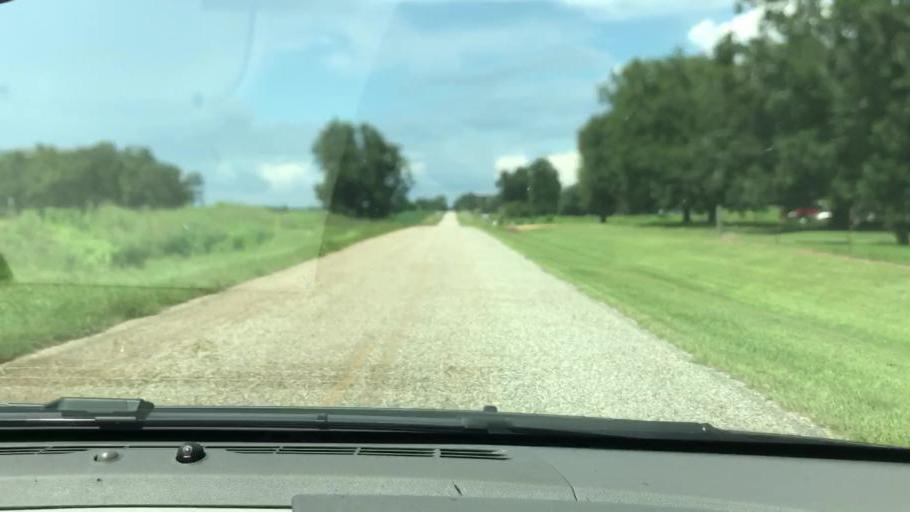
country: US
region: Georgia
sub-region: Early County
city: Blakely
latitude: 31.1934
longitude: -85.0039
